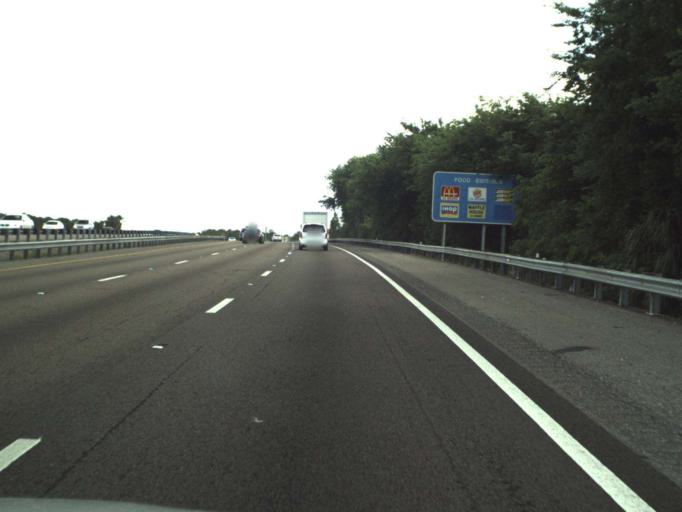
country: US
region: Florida
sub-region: Volusia County
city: DeBary
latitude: 28.8696
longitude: -81.2853
